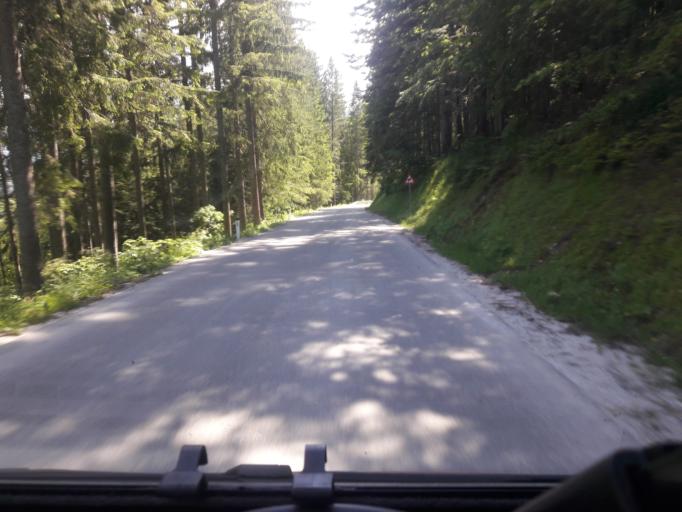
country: AT
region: Styria
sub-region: Politischer Bezirk Liezen
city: Tauplitz
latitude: 47.5716
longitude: 13.9610
